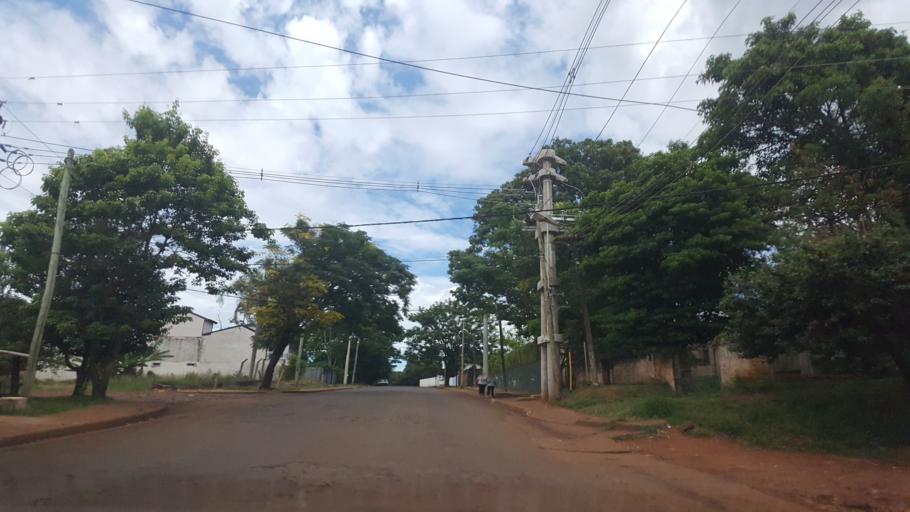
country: AR
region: Misiones
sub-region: Departamento de Capital
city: Posadas
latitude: -27.4285
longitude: -55.8894
